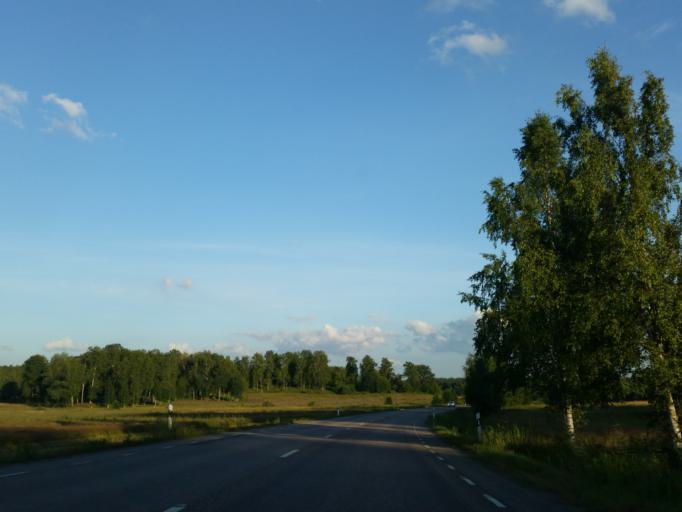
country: SE
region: Stockholm
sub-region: Sodertalje Kommun
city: Soedertaelje
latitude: 59.2271
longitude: 17.5606
